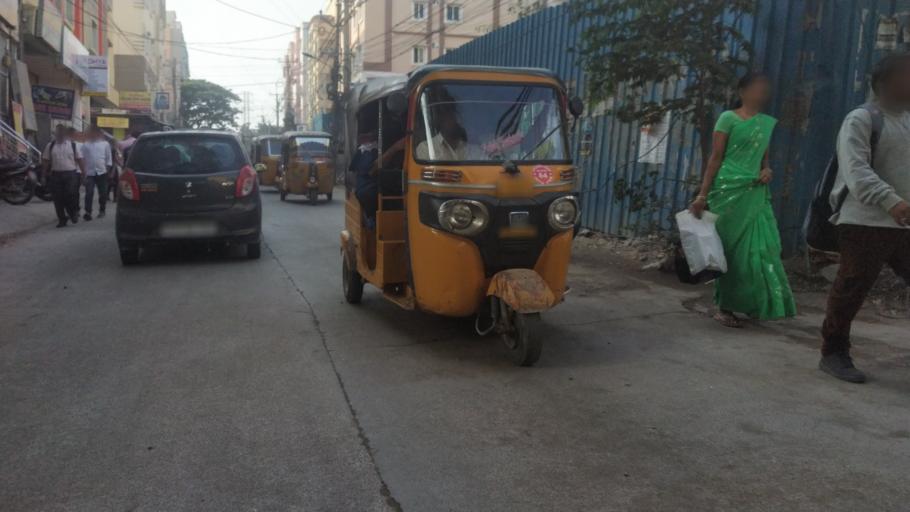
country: IN
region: Telangana
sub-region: Rangareddi
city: Kukatpalli
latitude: 17.4988
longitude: 78.3953
